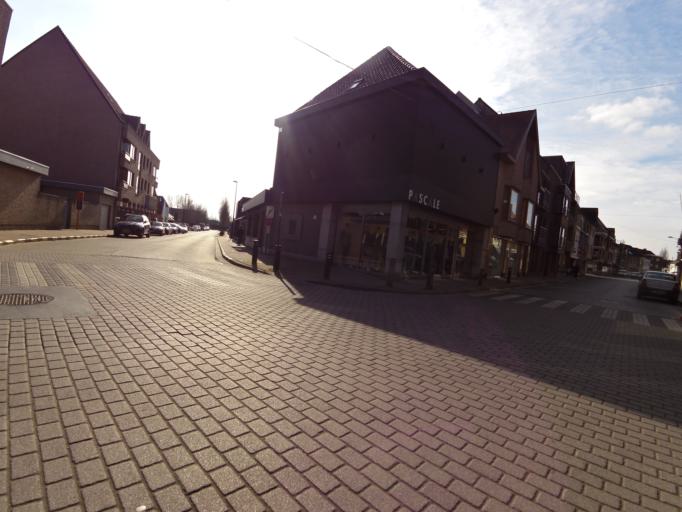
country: BE
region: Flanders
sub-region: Provincie West-Vlaanderen
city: Torhout
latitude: 51.0657
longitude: 3.0985
